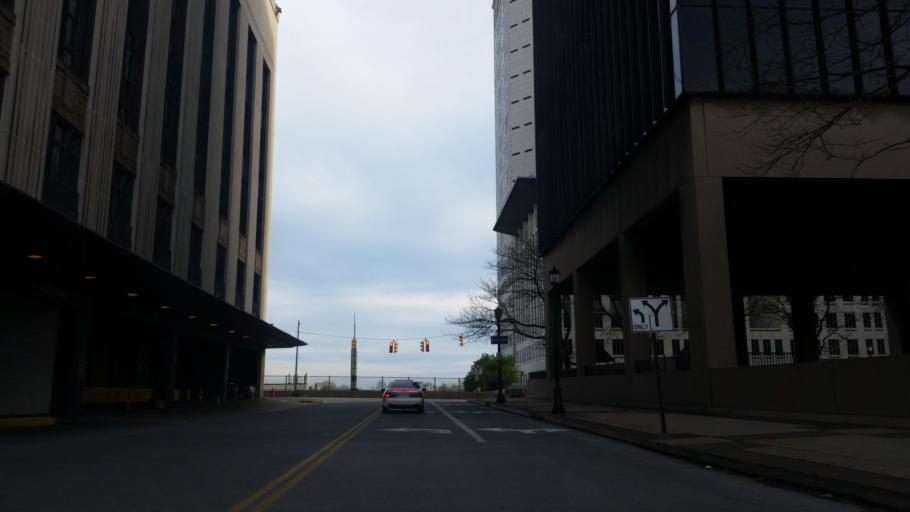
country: US
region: Ohio
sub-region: Cuyahoga County
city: Cleveland
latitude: 41.4977
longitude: -81.6967
